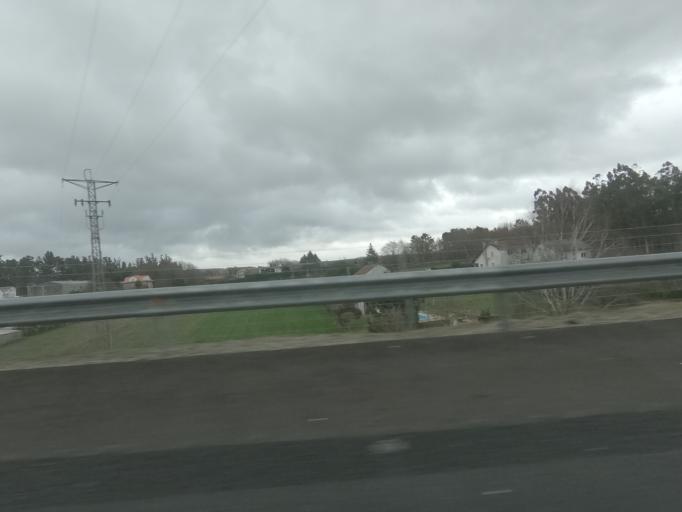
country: ES
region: Galicia
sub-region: Provincia da Coruna
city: Vedra
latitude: 42.8177
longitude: -8.4878
